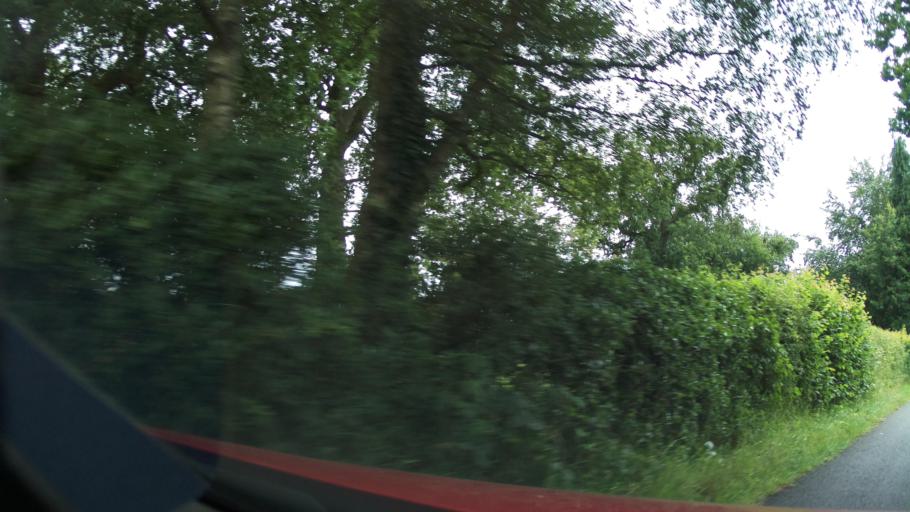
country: GB
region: England
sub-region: Solihull
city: Dickens Heath
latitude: 52.3779
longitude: -1.8401
